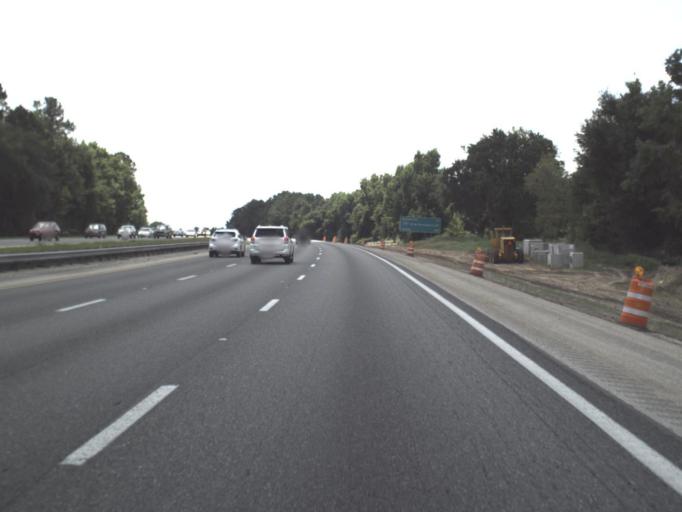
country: US
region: Florida
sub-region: Alachua County
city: High Springs
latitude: 29.7916
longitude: -82.5154
